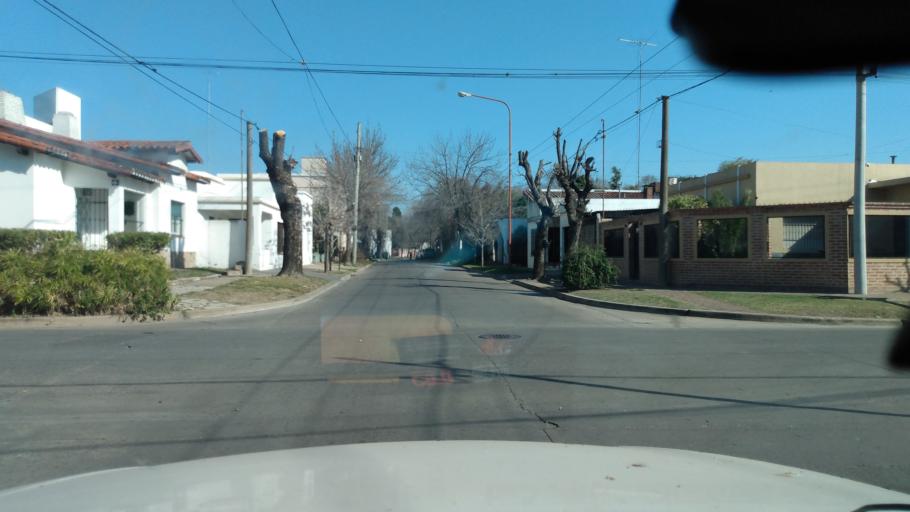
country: AR
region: Buenos Aires
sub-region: Partido de Lujan
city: Lujan
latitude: -34.5728
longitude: -59.1090
